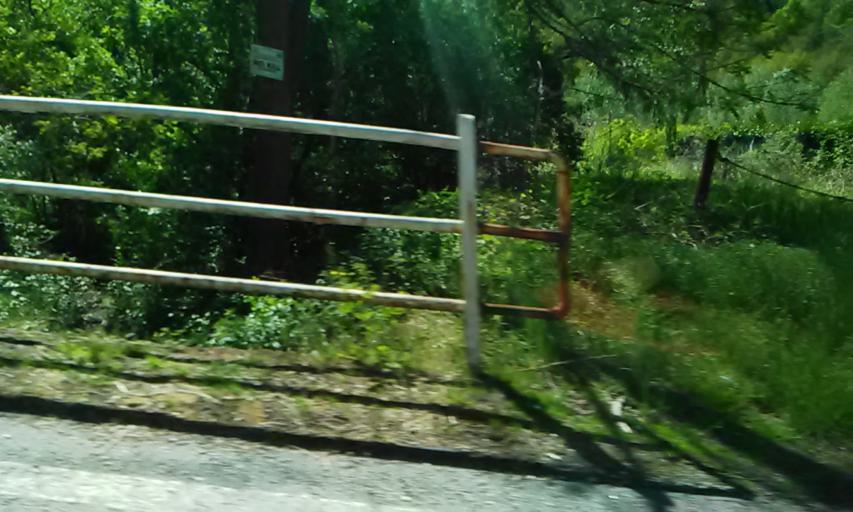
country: IT
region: Piedmont
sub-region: Provincia di Biella
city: Pray
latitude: 45.6762
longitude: 8.2277
